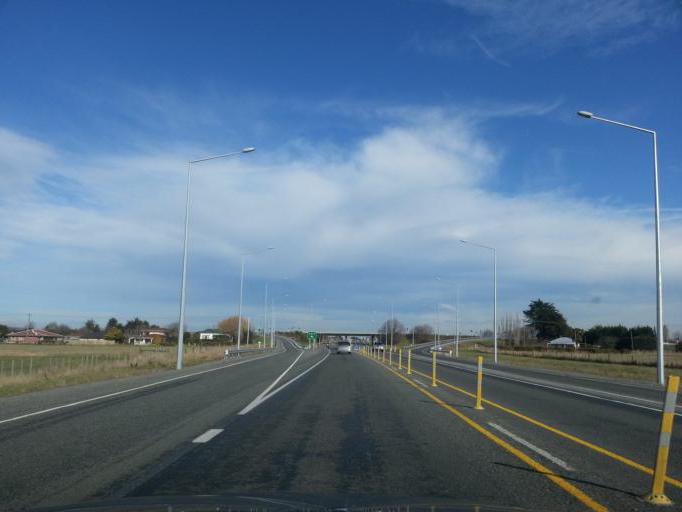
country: NZ
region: Canterbury
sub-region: Waimakariri District
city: Kaiapoi
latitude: -43.3710
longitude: 172.6482
